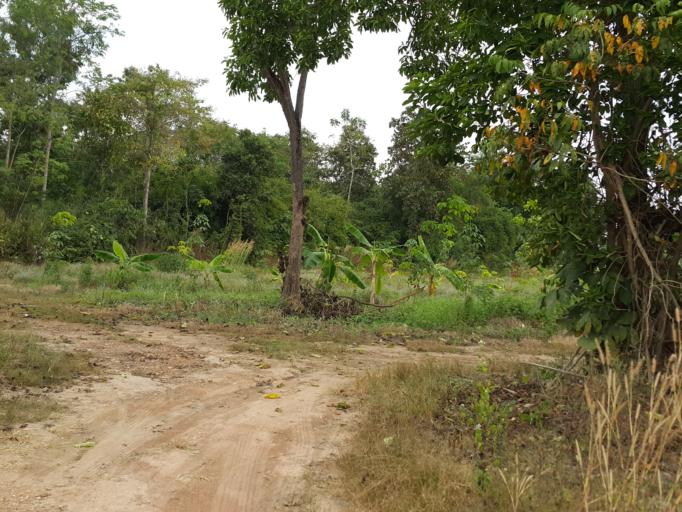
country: TH
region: Sukhothai
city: Thung Saliam
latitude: 17.3983
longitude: 99.5876
